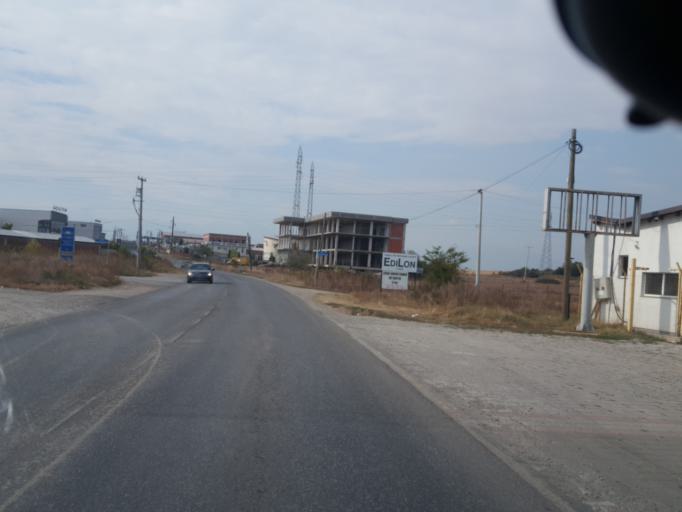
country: XK
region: Gjakova
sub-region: Komuna e Gjakoves
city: Gjakove
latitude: 42.3666
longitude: 20.4655
